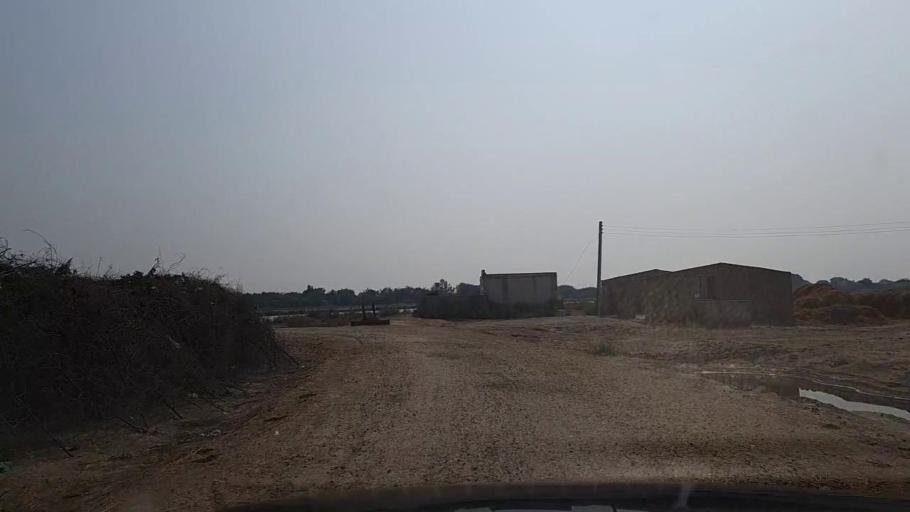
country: PK
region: Sindh
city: Mirpur Batoro
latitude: 24.6853
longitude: 68.2224
